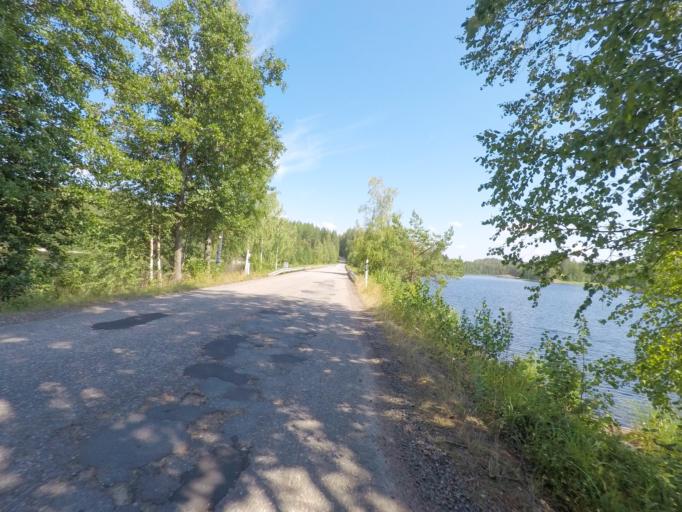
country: FI
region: Southern Savonia
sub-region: Mikkeli
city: Puumala
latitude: 61.4056
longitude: 28.0766
